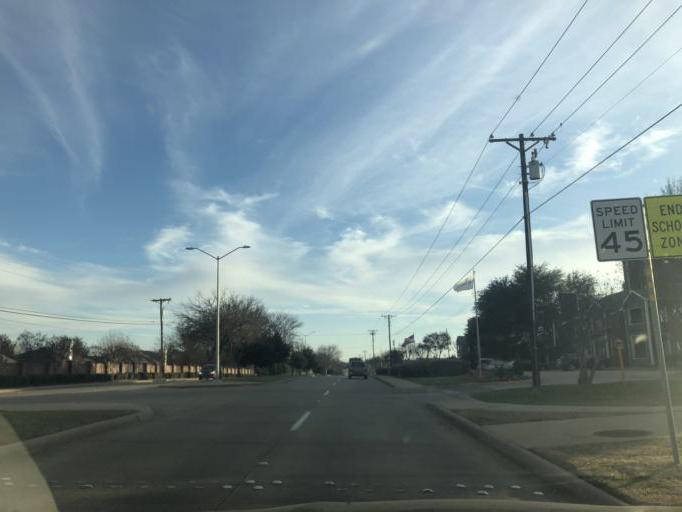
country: US
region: Texas
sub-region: Dallas County
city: Cedar Hill
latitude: 32.5943
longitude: -96.9255
